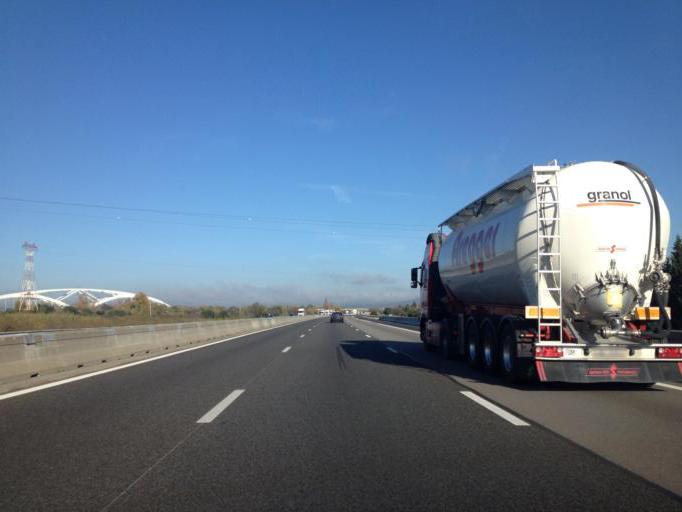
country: FR
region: Rhone-Alpes
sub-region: Departement de la Drome
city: Pierrelatte
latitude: 44.3686
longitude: 4.7344
